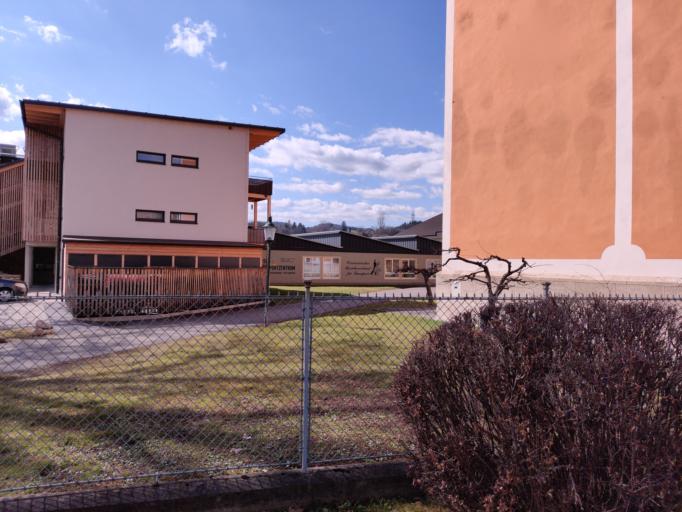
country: AT
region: Styria
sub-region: Politischer Bezirk Voitsberg
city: Voitsberg
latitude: 47.0511
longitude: 15.1440
